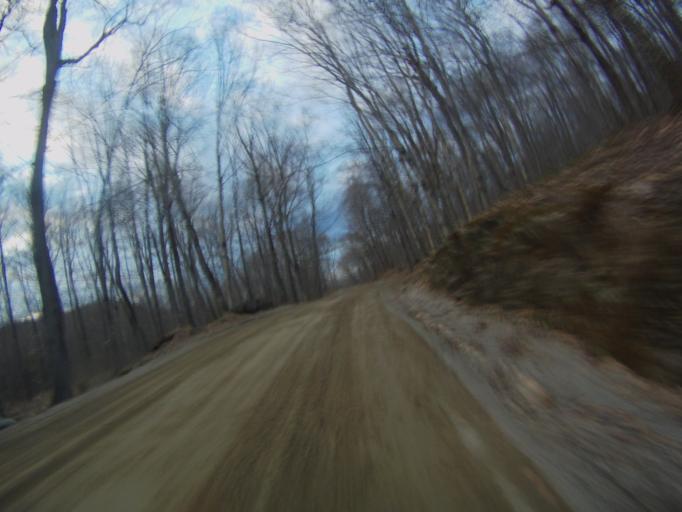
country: US
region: Vermont
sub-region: Rutland County
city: Brandon
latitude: 43.9304
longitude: -73.0205
